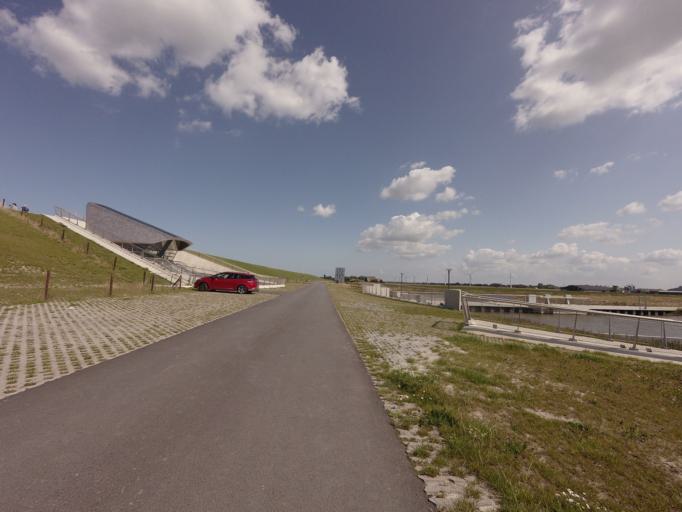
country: NL
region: Friesland
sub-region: Gemeente Ferwerderadiel
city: Hallum
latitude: 53.3210
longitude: 5.7589
